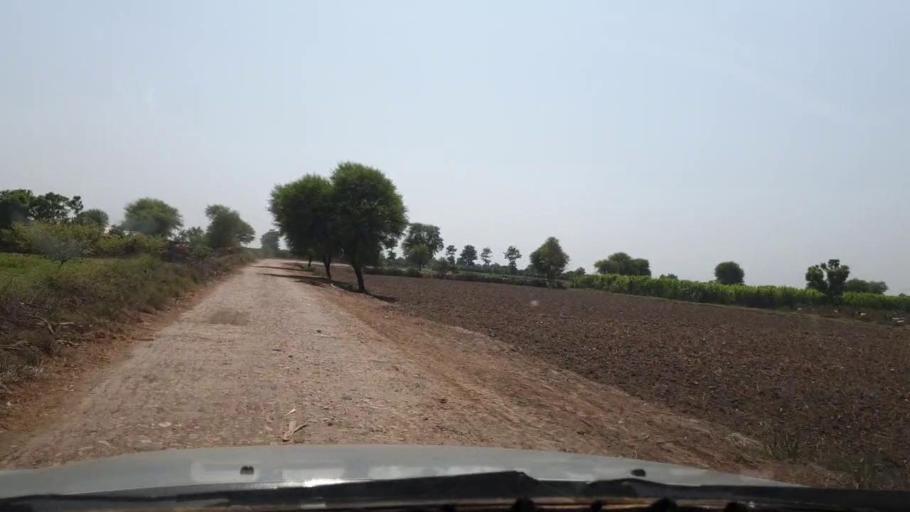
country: PK
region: Sindh
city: Tando Muhammad Khan
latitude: 25.1982
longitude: 68.6628
